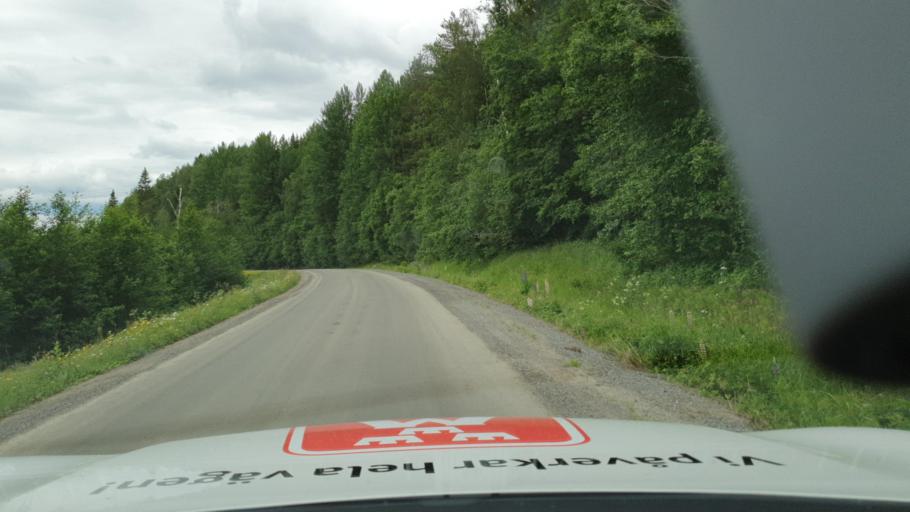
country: SE
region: Vaesterbotten
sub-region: Nordmalings Kommun
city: Nordmaling
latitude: 63.6852
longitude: 19.4506
